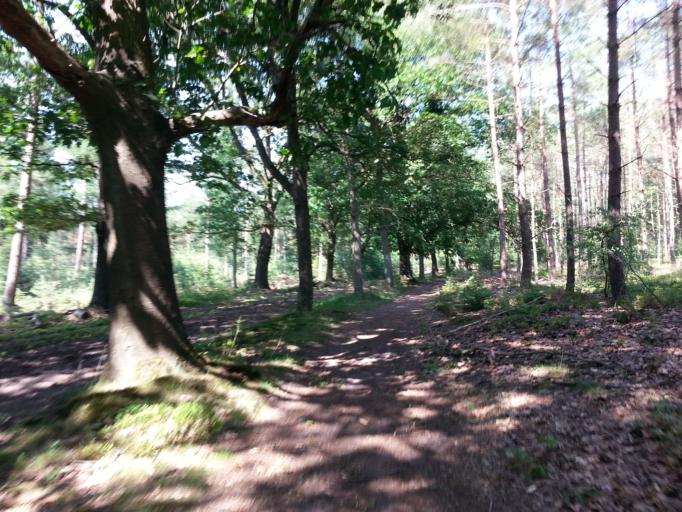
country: NL
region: Utrecht
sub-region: Gemeente Amersfoort
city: Randenbroek
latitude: 52.1122
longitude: 5.3812
